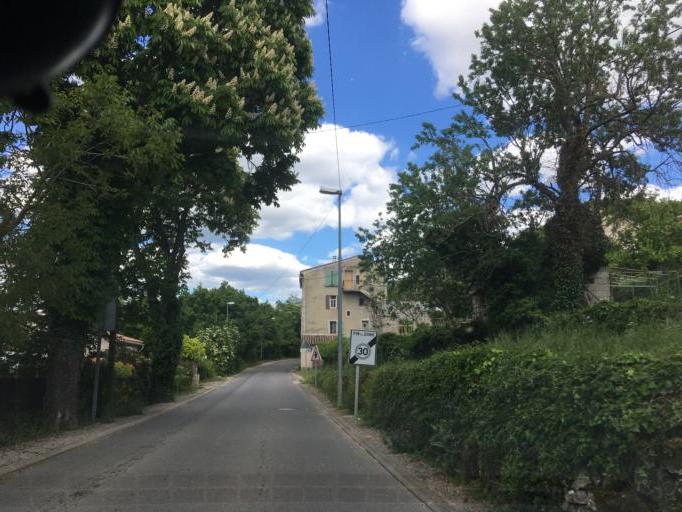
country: FR
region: Provence-Alpes-Cote d'Azur
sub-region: Departement du Var
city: Ginasservis
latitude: 43.5928
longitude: 5.8483
